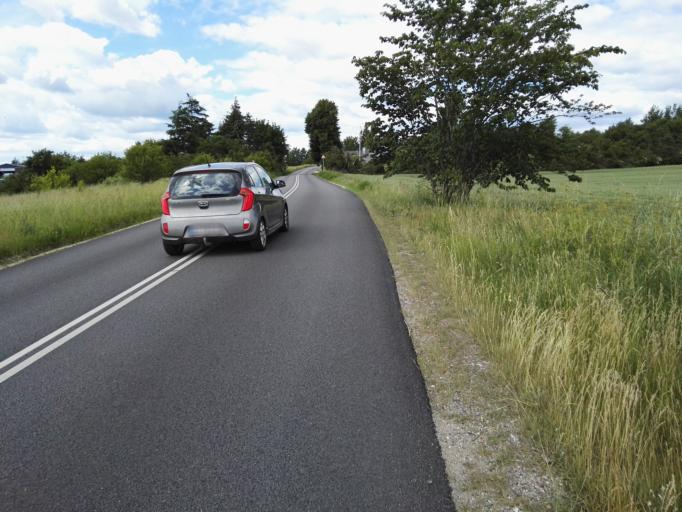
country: DK
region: Capital Region
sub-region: Egedal Kommune
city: Olstykke
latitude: 55.7676
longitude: 12.1489
